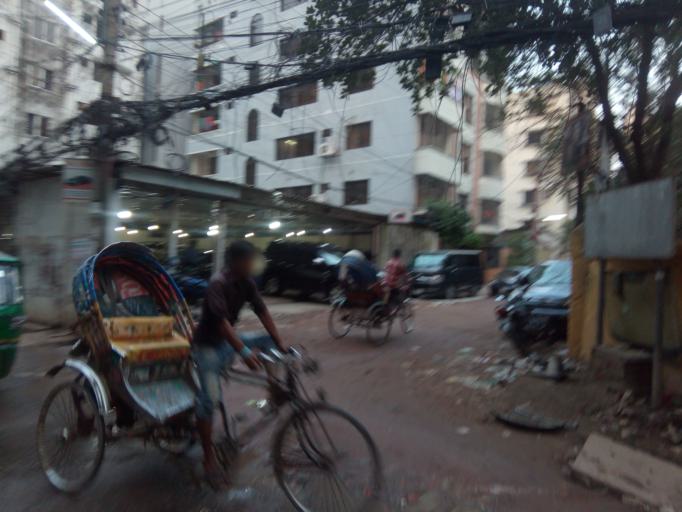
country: BD
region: Dhaka
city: Paltan
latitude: 23.7849
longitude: 90.4001
